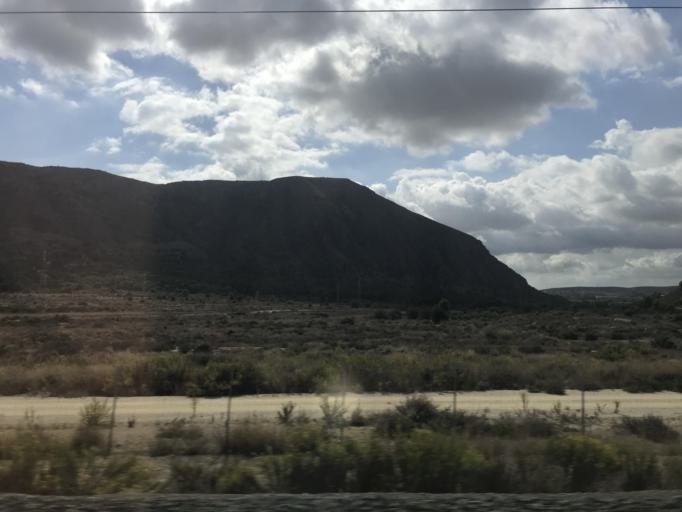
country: ES
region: Valencia
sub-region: Provincia de Alicante
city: San Vicent del Raspeig
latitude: 38.3654
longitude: -0.5927
